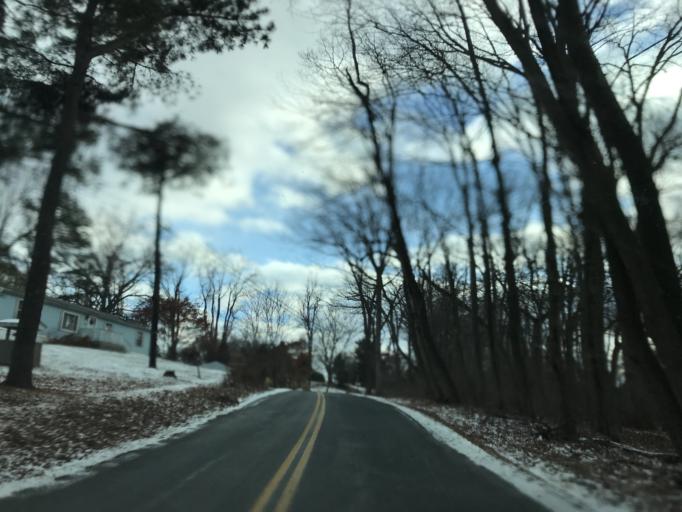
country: US
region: Maryland
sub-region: Harford County
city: Jarrettsville
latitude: 39.6273
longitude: -76.4795
